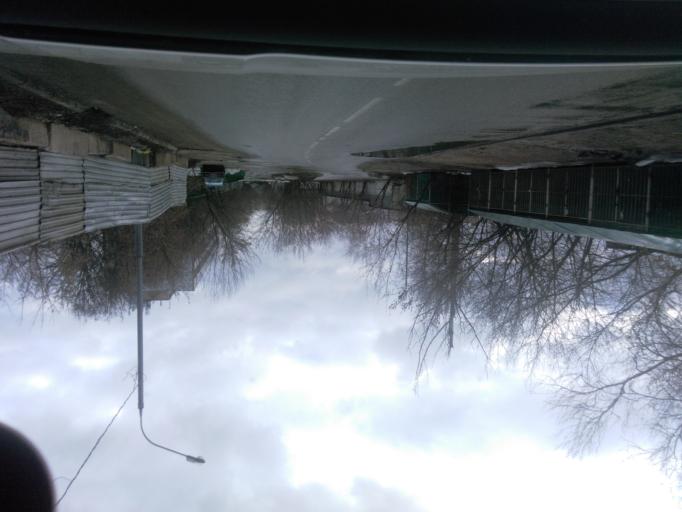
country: RU
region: Moskovskaya
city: Koptevo
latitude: 55.8211
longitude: 37.5320
